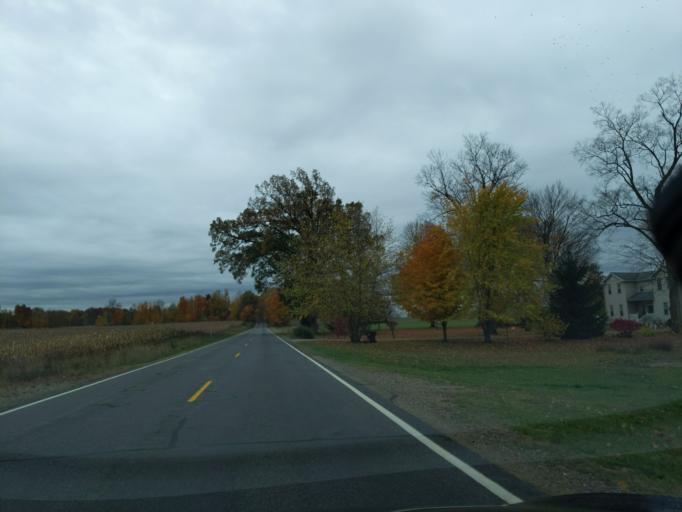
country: US
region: Michigan
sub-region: Jackson County
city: Spring Arbor
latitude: 42.3096
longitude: -84.6003
